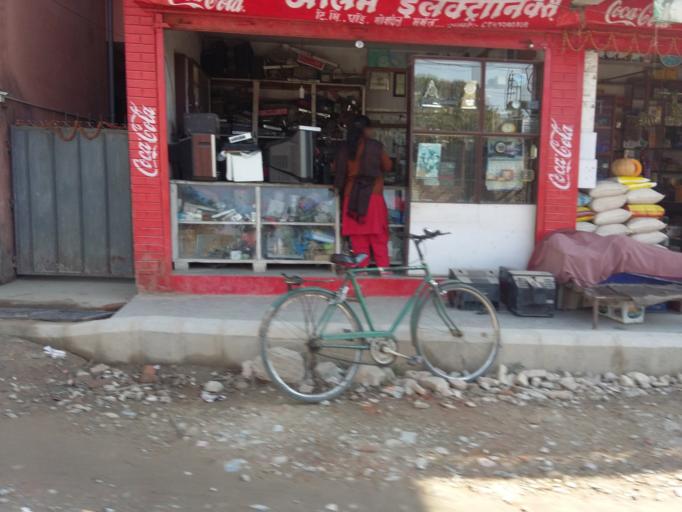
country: NP
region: Central Region
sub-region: Bagmati Zone
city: Kathmandu
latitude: 27.7244
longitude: 85.3372
